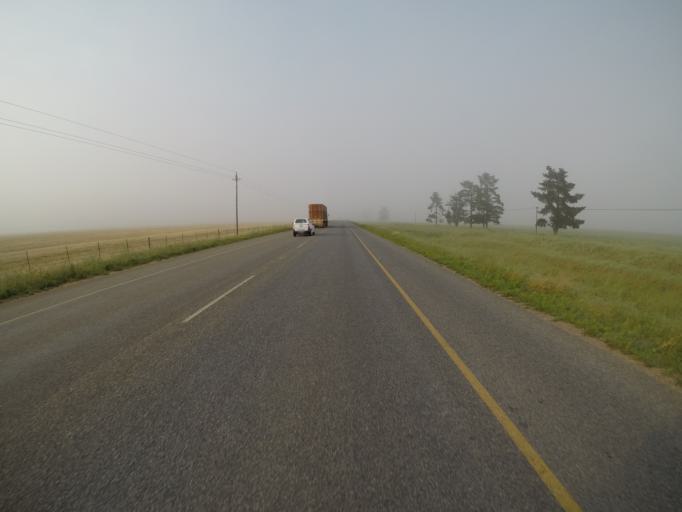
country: ZA
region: Western Cape
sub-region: City of Cape Town
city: Kraaifontein
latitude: -33.6696
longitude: 18.7073
